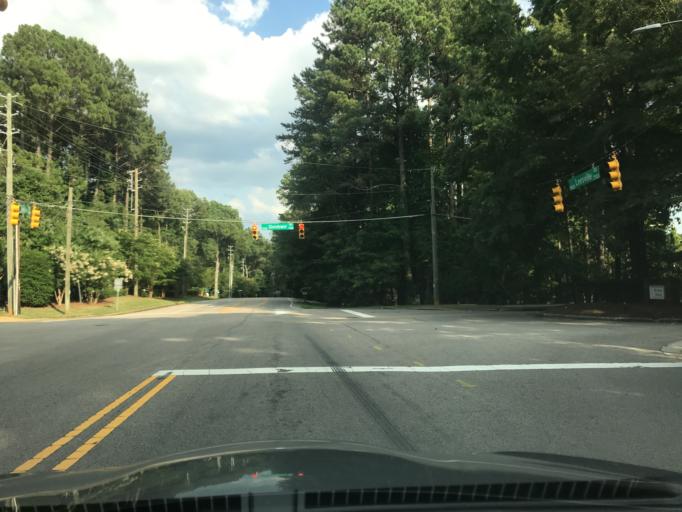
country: US
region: North Carolina
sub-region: Wake County
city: West Raleigh
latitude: 35.8785
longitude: -78.7057
